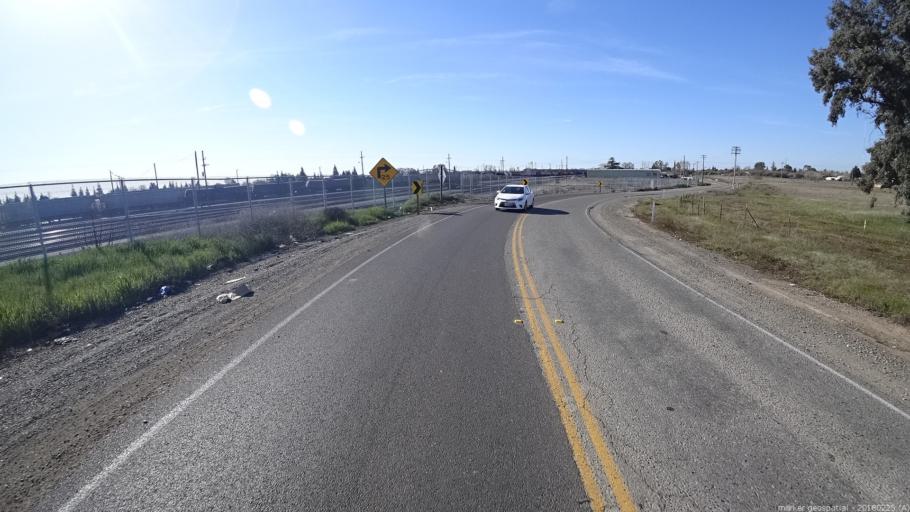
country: US
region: California
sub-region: Sacramento County
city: Antelope
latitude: 38.7118
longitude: -121.3275
